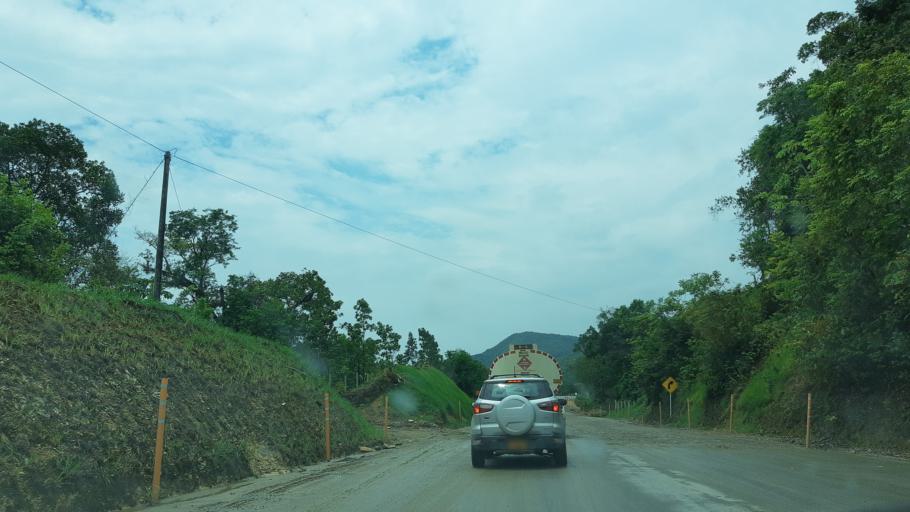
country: CO
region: Casanare
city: Sabanalarga
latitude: 4.7692
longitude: -73.0047
